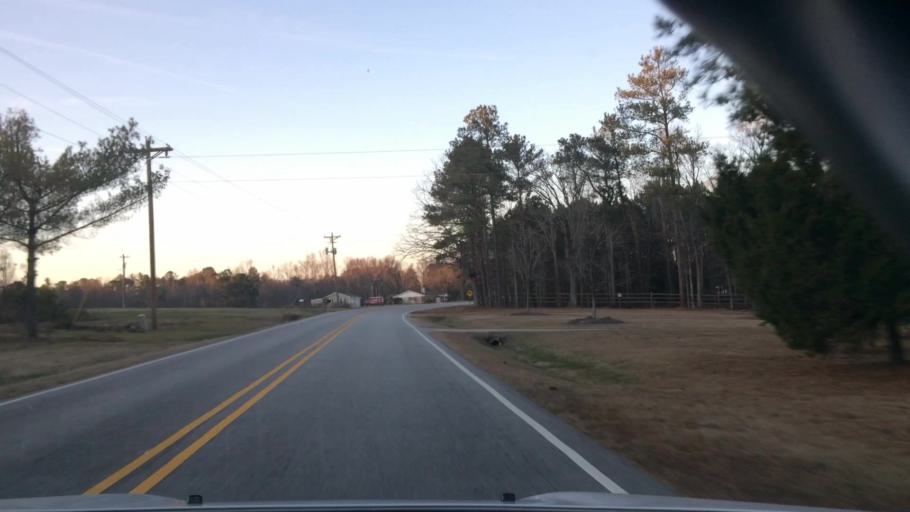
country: US
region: North Carolina
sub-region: Franklin County
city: Youngsville
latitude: 35.9892
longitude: -78.4177
